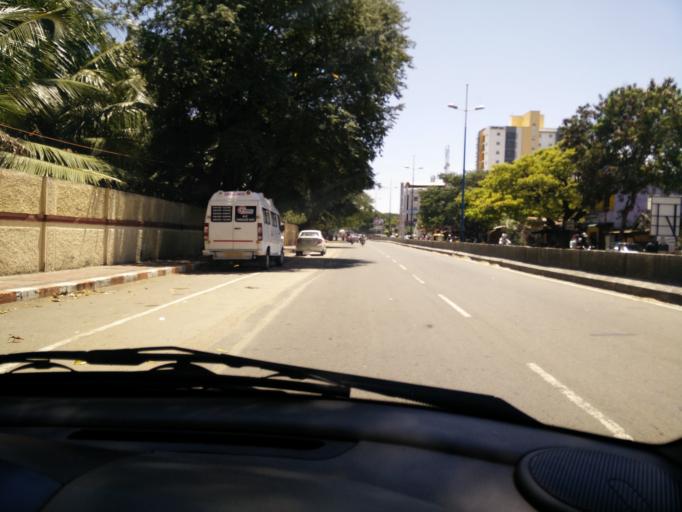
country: IN
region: Tamil Nadu
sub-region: Coimbatore
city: Coimbatore
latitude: 10.9951
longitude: 76.9731
